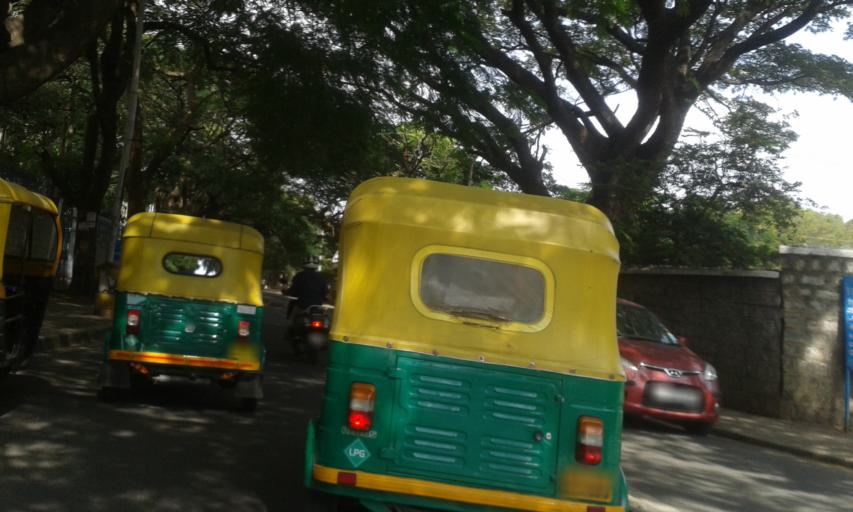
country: IN
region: Karnataka
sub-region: Bangalore Urban
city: Bangalore
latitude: 12.9649
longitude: 77.6280
